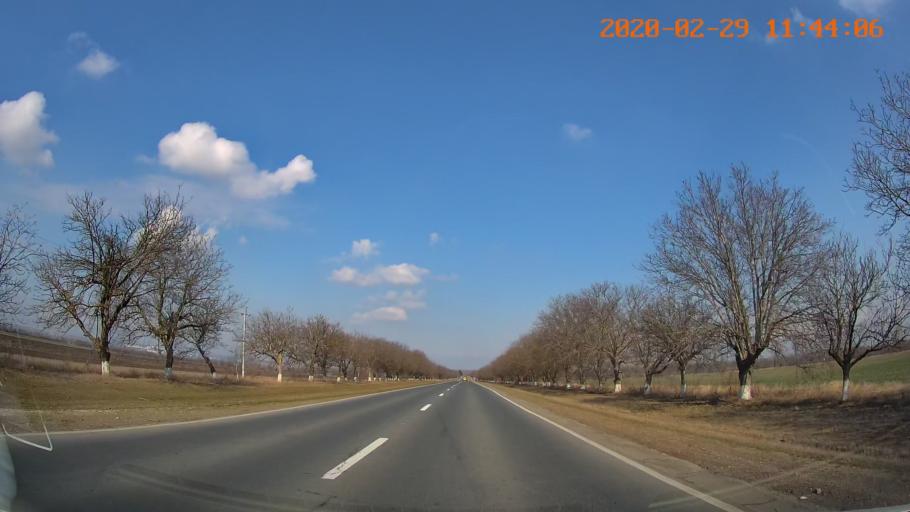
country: MD
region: Rezina
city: Saharna
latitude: 47.7062
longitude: 29.0010
